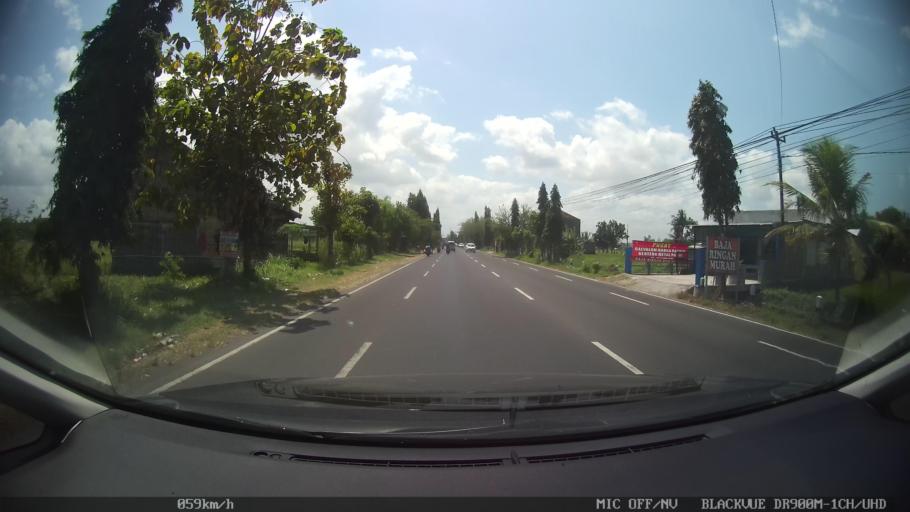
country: ID
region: Daerah Istimewa Yogyakarta
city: Pandak
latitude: -7.9263
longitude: 110.2777
